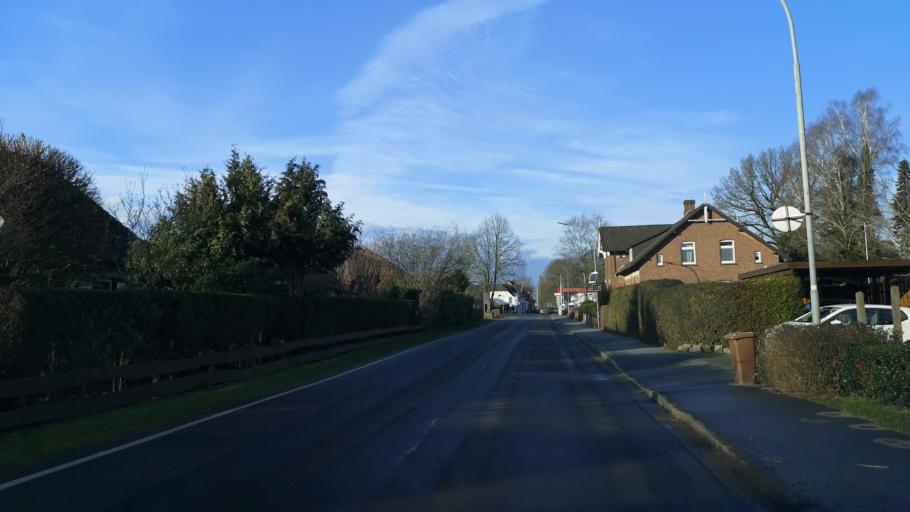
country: DE
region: Schleswig-Holstein
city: Lagerdorf
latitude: 53.8839
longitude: 9.5802
